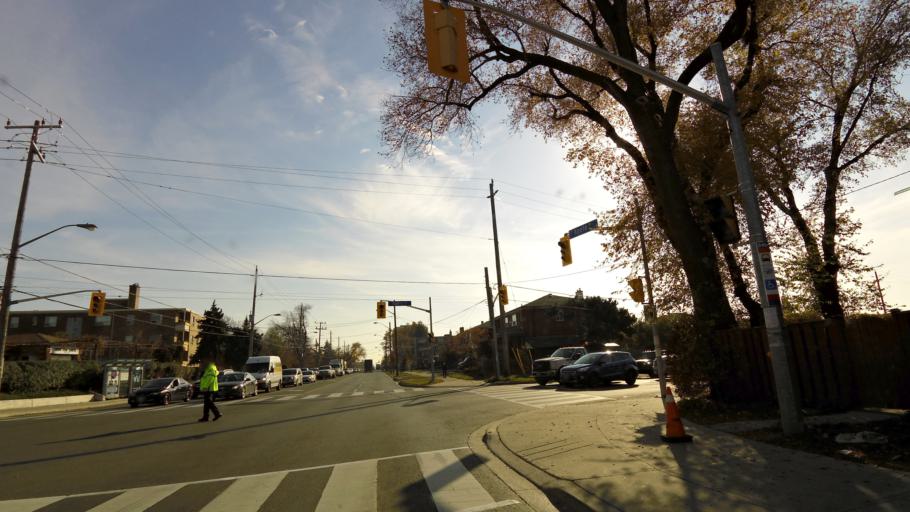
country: CA
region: Ontario
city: Toronto
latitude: 43.7180
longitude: -79.4801
